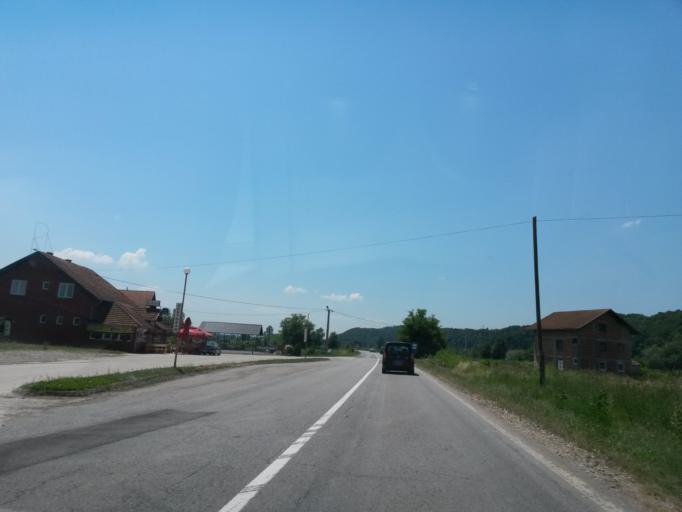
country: BA
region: Federation of Bosnia and Herzegovina
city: Lukavica
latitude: 44.9004
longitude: 18.0977
